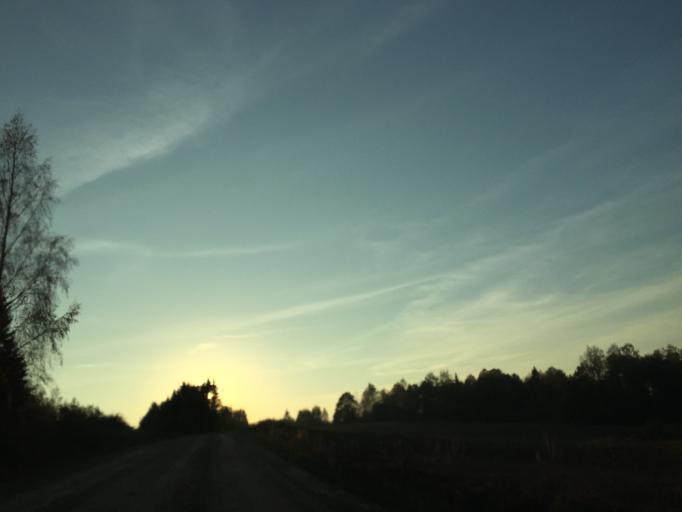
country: LV
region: Vainode
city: Vainode
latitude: 56.4900
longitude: 21.7893
